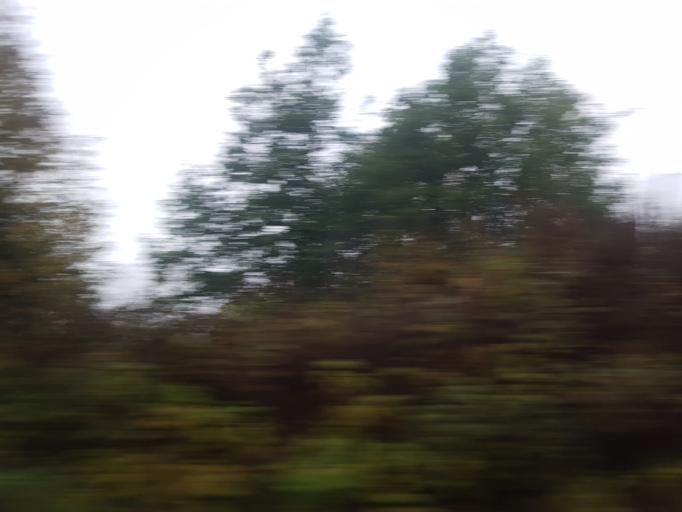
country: NO
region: Sor-Trondelag
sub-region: Trondheim
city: Trondheim
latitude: 63.3724
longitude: 10.3601
